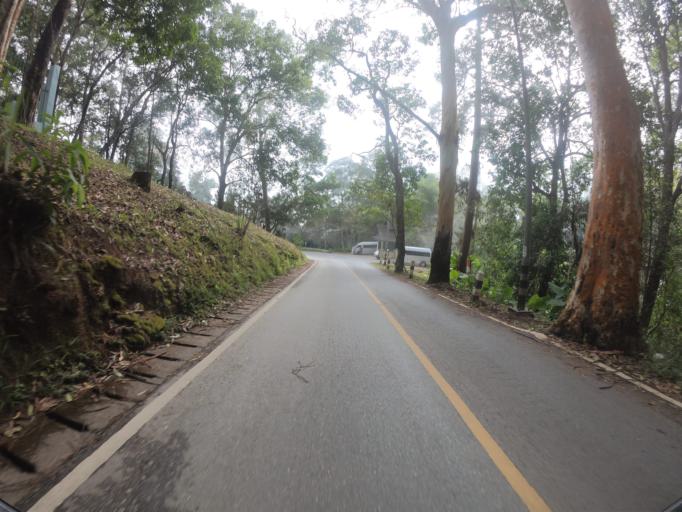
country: TH
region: Chiang Mai
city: Chiang Mai
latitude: 18.8036
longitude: 98.8980
